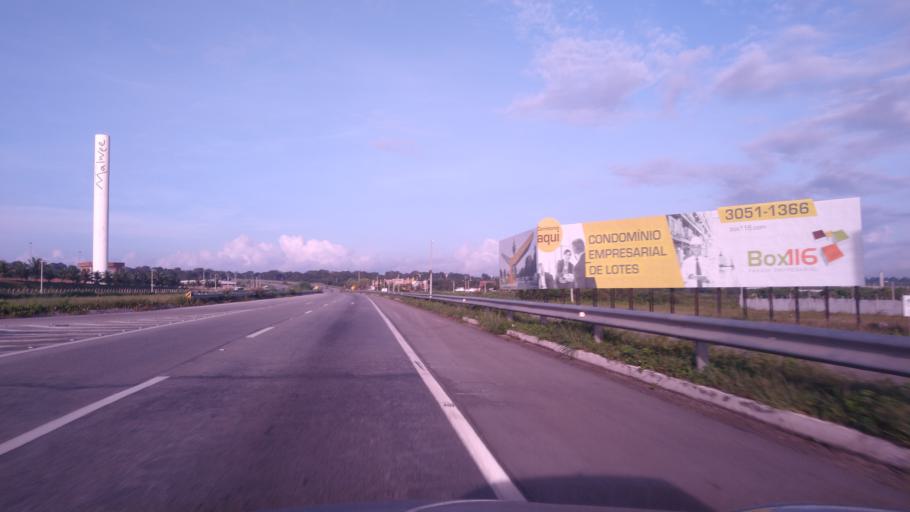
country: BR
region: Ceara
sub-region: Pacajus
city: Pacajus
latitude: -4.1640
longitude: -38.4883
